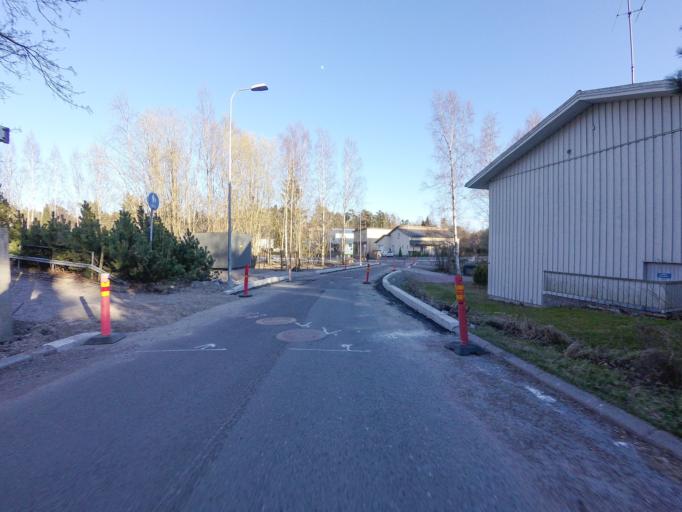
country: FI
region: Uusimaa
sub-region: Helsinki
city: Helsinki
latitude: 60.1738
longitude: 25.0206
